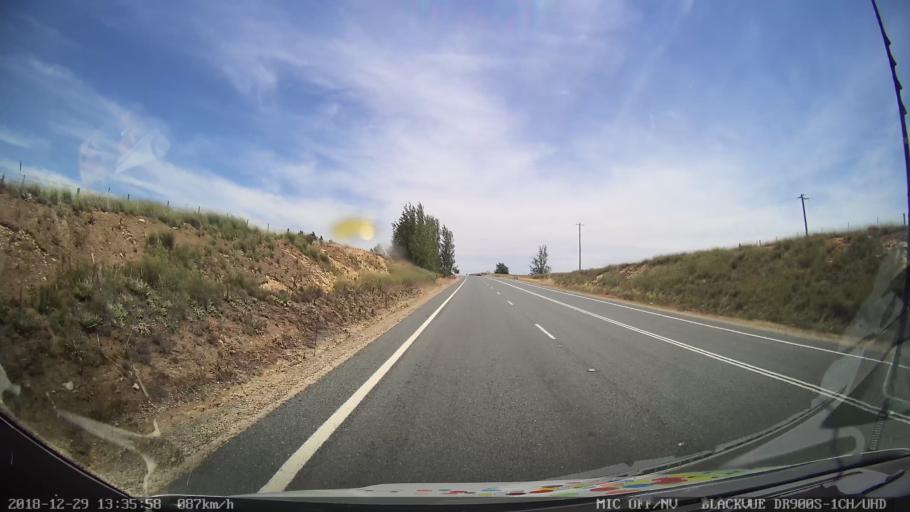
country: AU
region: New South Wales
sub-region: Cooma-Monaro
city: Cooma
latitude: -35.9656
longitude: 149.1456
